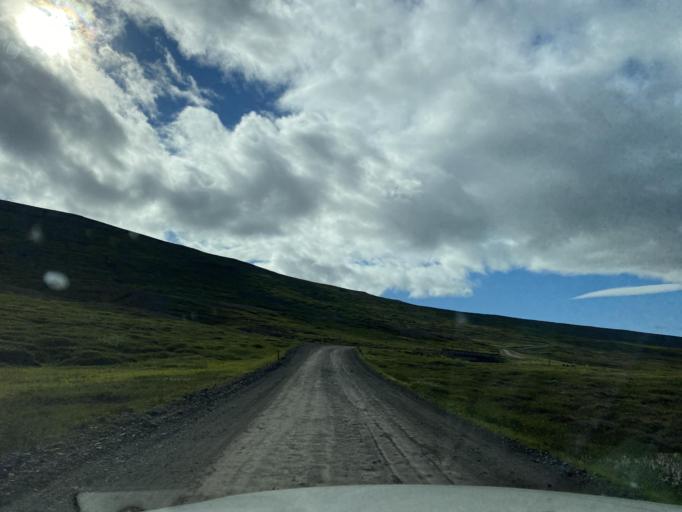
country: IS
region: East
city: Egilsstadir
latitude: 65.1869
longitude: -14.3281
